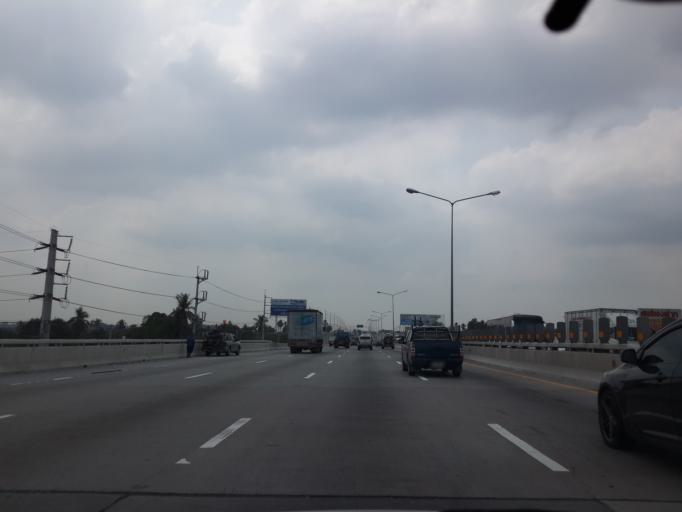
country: TH
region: Chon Buri
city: Si Racha
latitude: 13.1817
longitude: 100.9957
